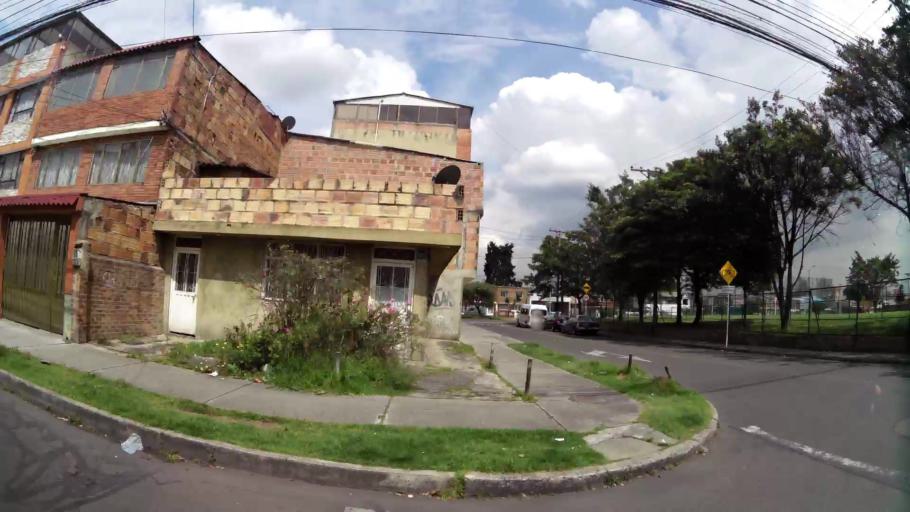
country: CO
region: Bogota D.C.
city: Bogota
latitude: 4.6094
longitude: -74.1169
